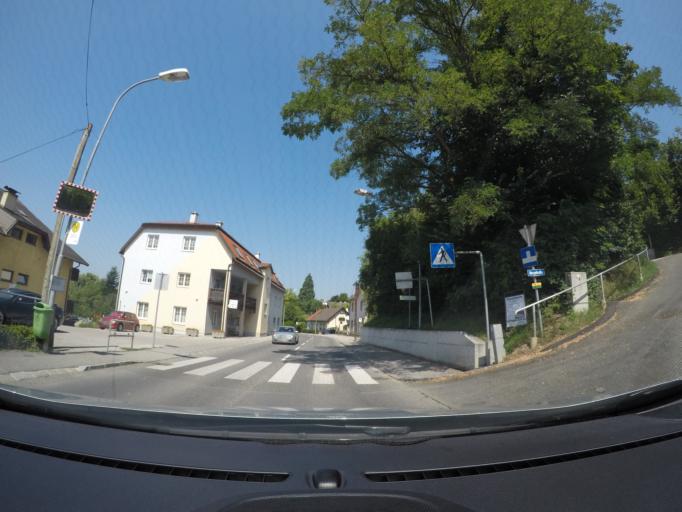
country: AT
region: Lower Austria
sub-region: Politischer Bezirk Sankt Polten
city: Eichgraben
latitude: 48.1796
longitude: 15.9851
